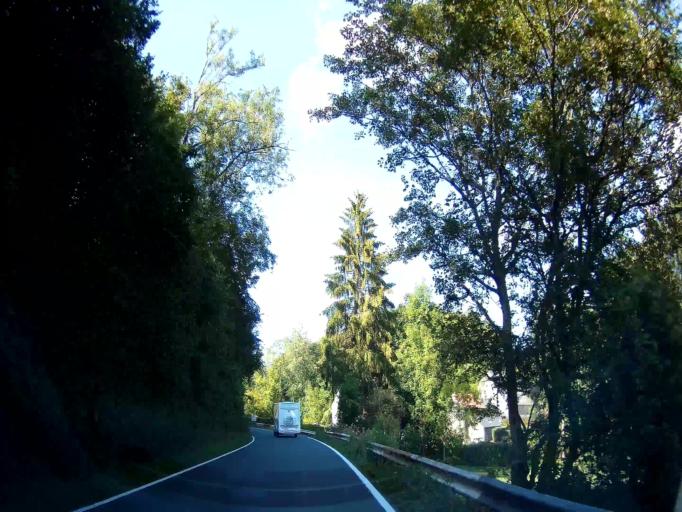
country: BE
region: Wallonia
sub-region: Province de Namur
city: Mettet
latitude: 50.3127
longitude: 4.7613
